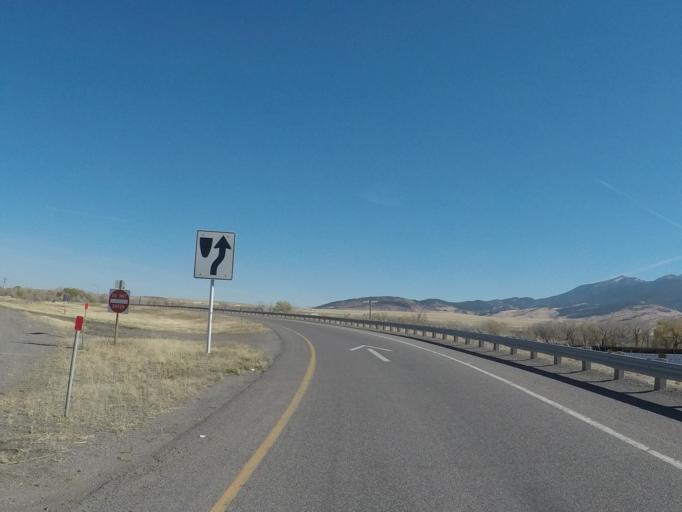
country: US
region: Montana
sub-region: Park County
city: Livingston
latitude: 45.6431
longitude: -110.5715
